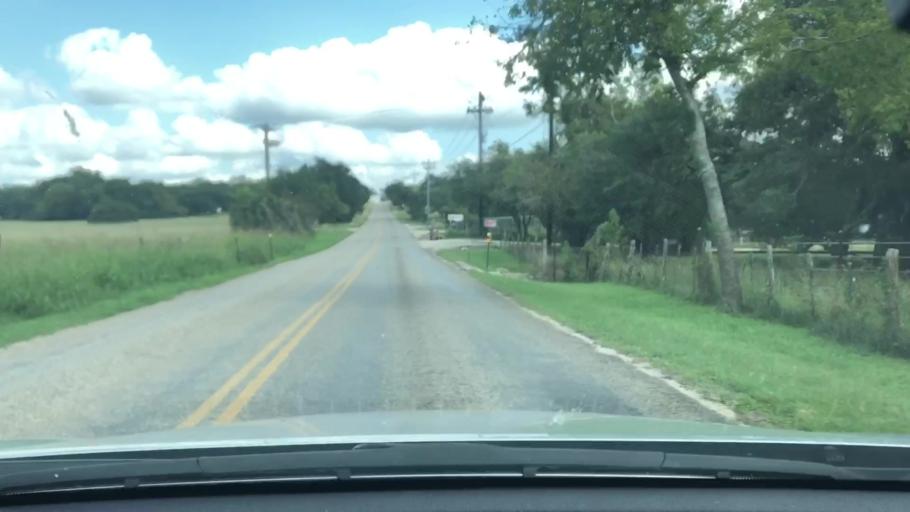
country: US
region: Texas
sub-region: Bexar County
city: Fair Oaks Ranch
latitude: 29.7860
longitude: -98.6673
